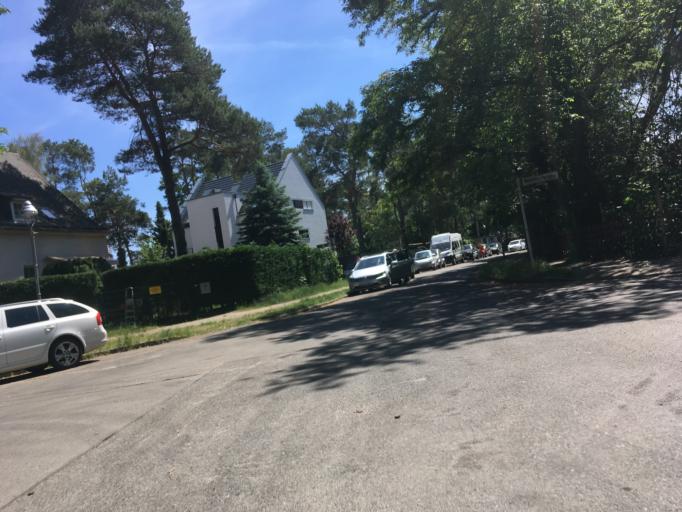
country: DE
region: Berlin
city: Schmockwitz
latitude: 52.3901
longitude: 13.6408
